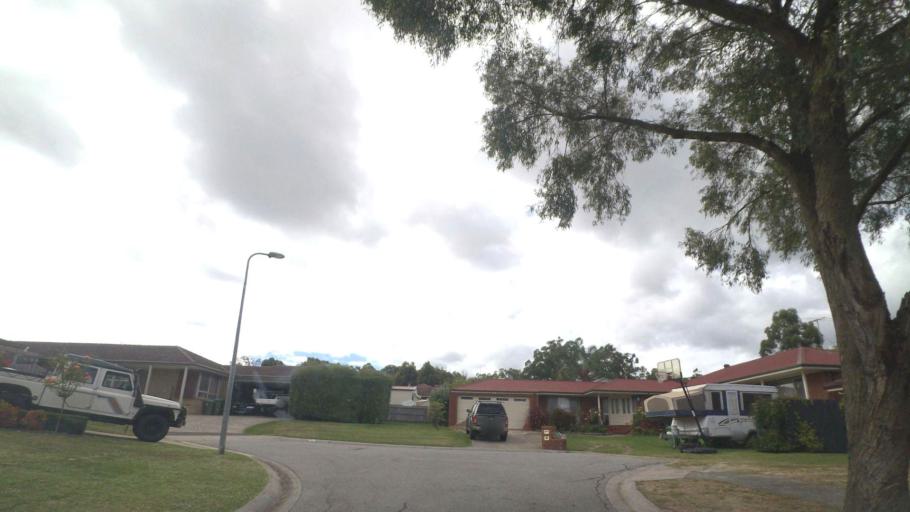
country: AU
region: Victoria
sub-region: Maroondah
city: Bayswater North
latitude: -37.8298
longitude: 145.3059
